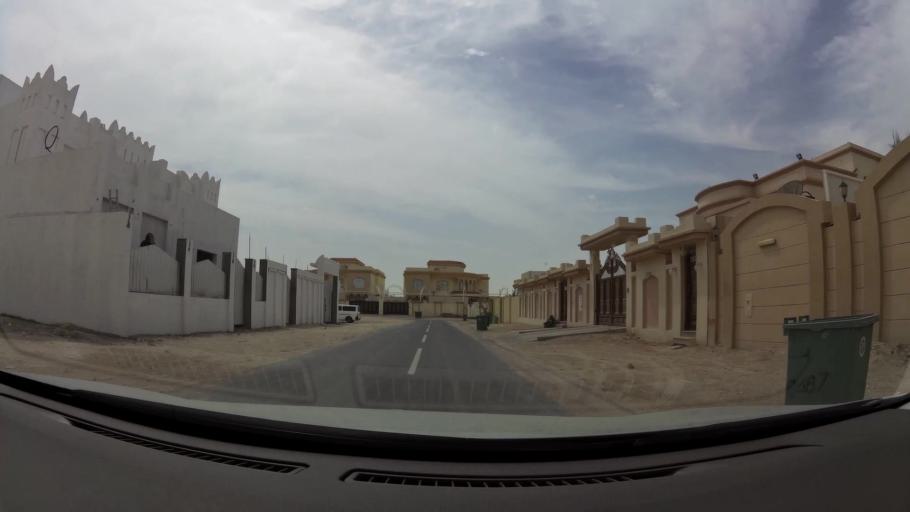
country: QA
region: Baladiyat ad Dawhah
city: Doha
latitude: 25.2098
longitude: 51.4698
